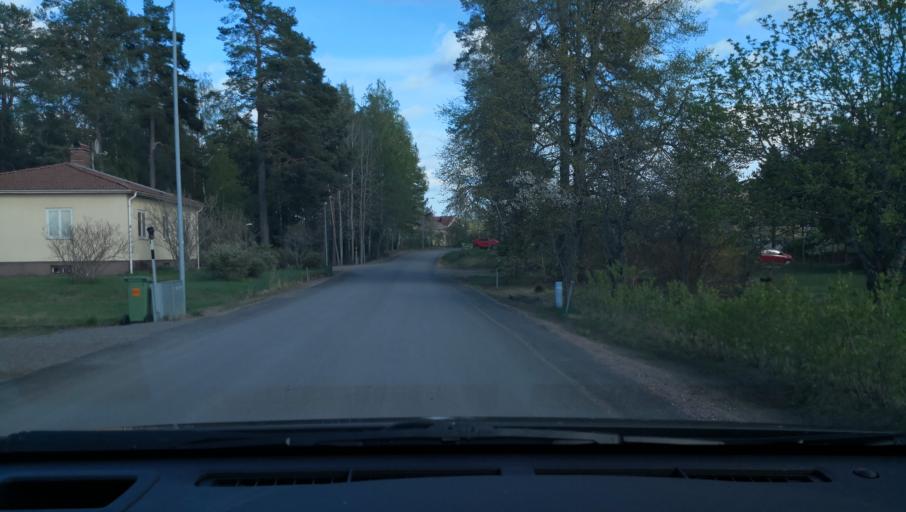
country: SE
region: OErebro
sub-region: Askersunds Kommun
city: Asbro
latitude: 58.9188
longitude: 15.0593
